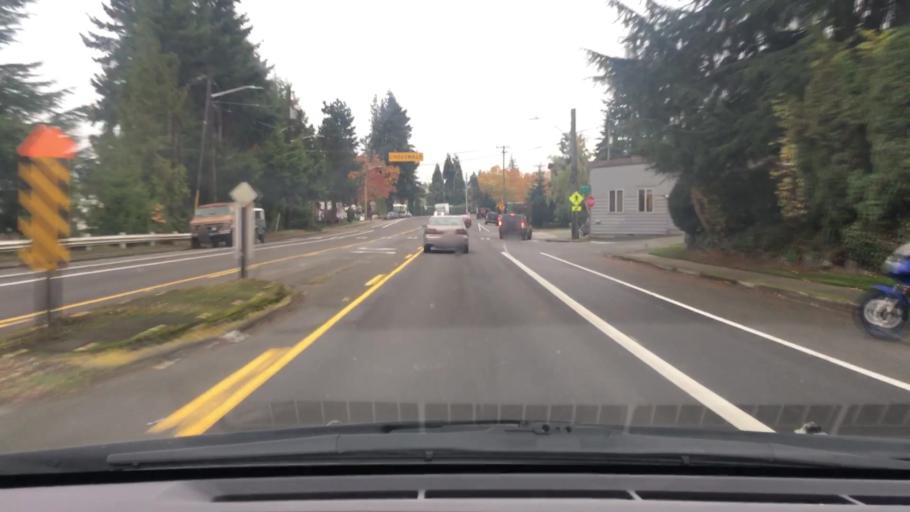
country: US
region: Washington
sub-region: King County
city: Bryn Mawr-Skyway
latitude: 47.5021
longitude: -122.2236
